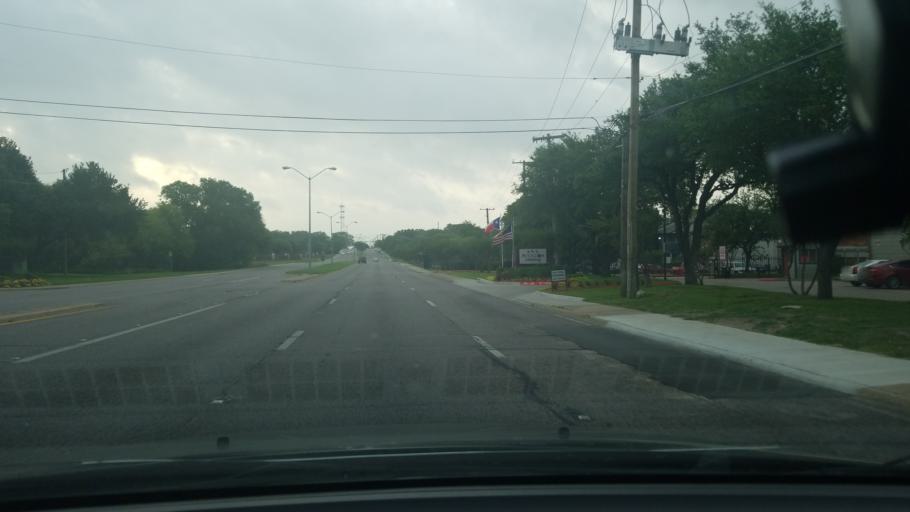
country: US
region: Texas
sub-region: Dallas County
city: Balch Springs
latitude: 32.7623
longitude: -96.6542
